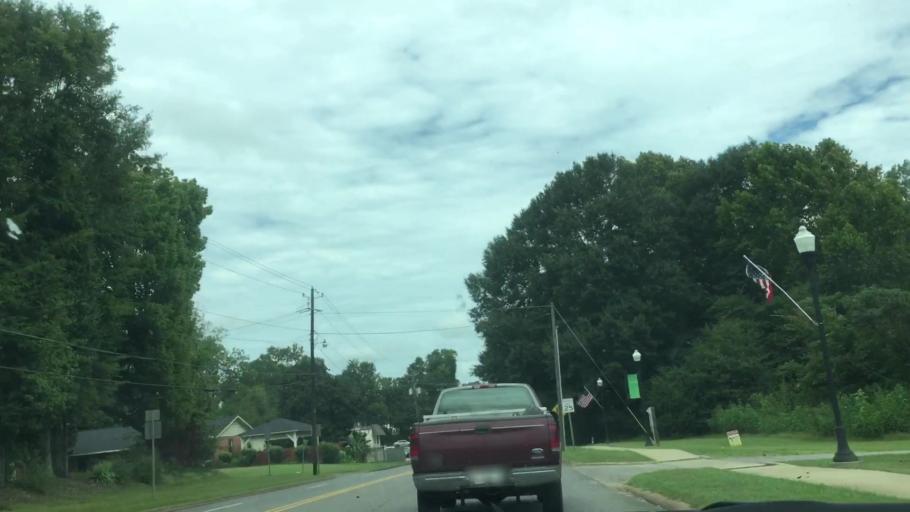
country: US
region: Alabama
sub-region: Hale County
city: Greensboro
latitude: 32.7011
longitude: -87.5954
